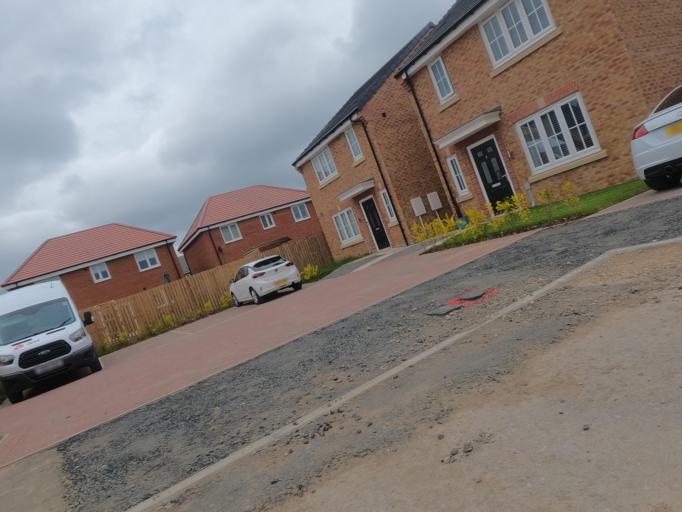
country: GB
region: England
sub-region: Northumberland
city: Blyth
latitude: 55.1058
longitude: -1.5355
